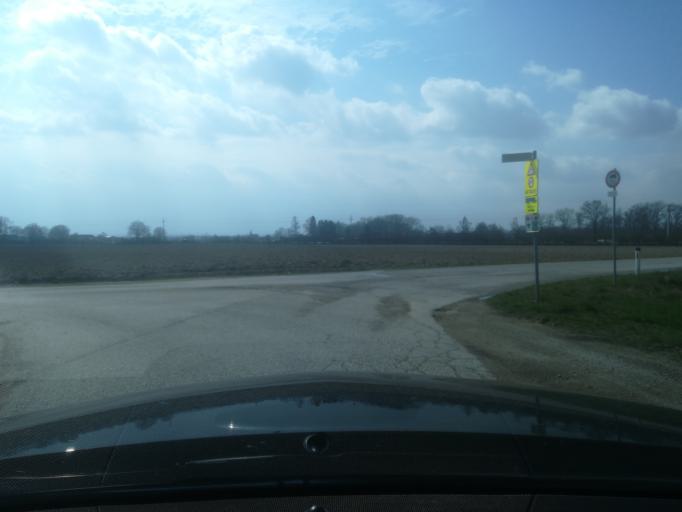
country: AT
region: Upper Austria
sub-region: Politischer Bezirk Perg
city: Perg
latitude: 48.2446
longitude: 14.6102
